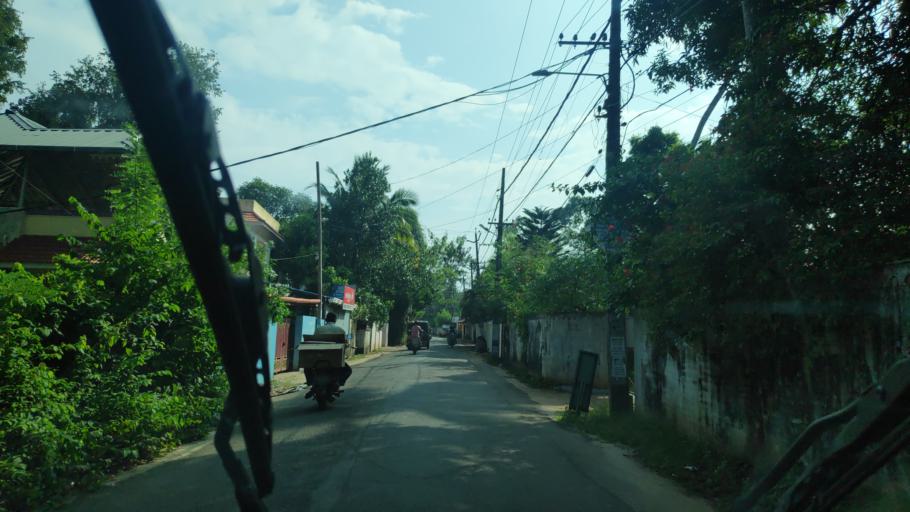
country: IN
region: Kerala
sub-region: Alappuzha
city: Alleppey
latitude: 9.5082
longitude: 76.3203
